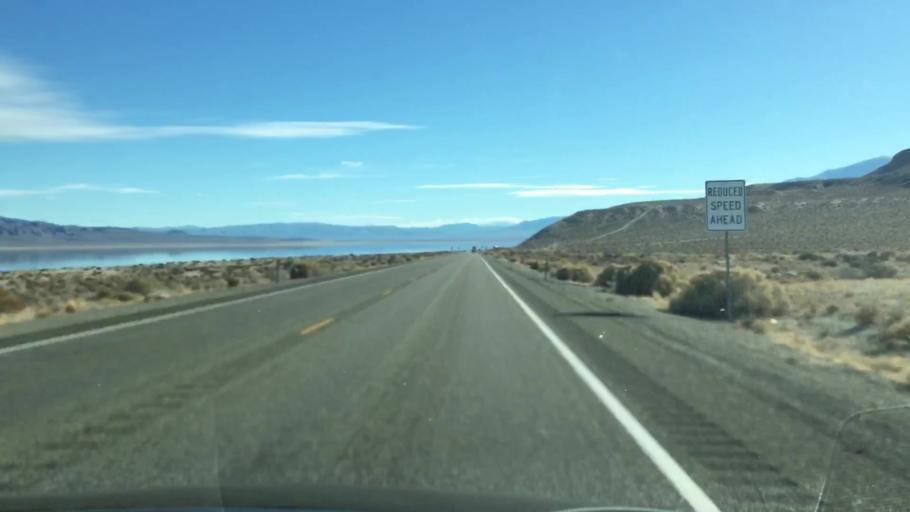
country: US
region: Nevada
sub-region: Mineral County
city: Hawthorne
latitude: 38.7900
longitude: -118.7549
